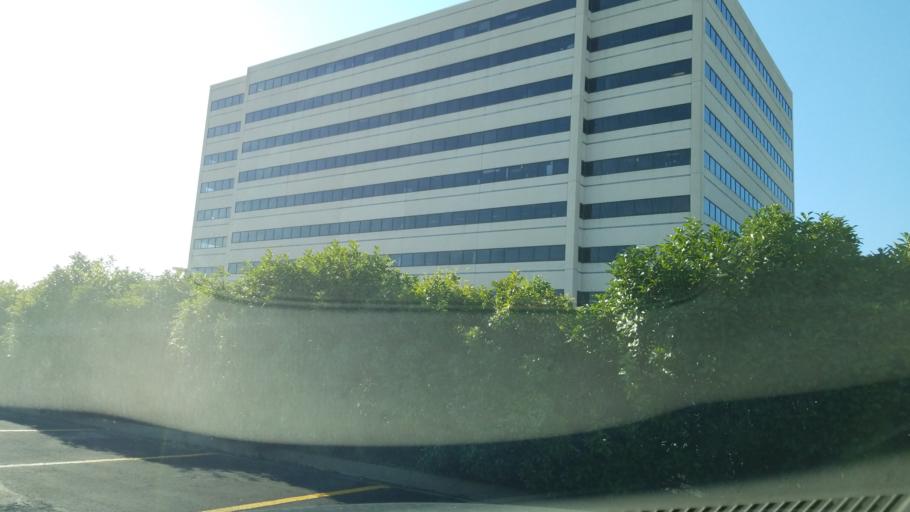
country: US
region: Texas
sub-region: Dallas County
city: Irving
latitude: 32.8885
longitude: -96.9696
